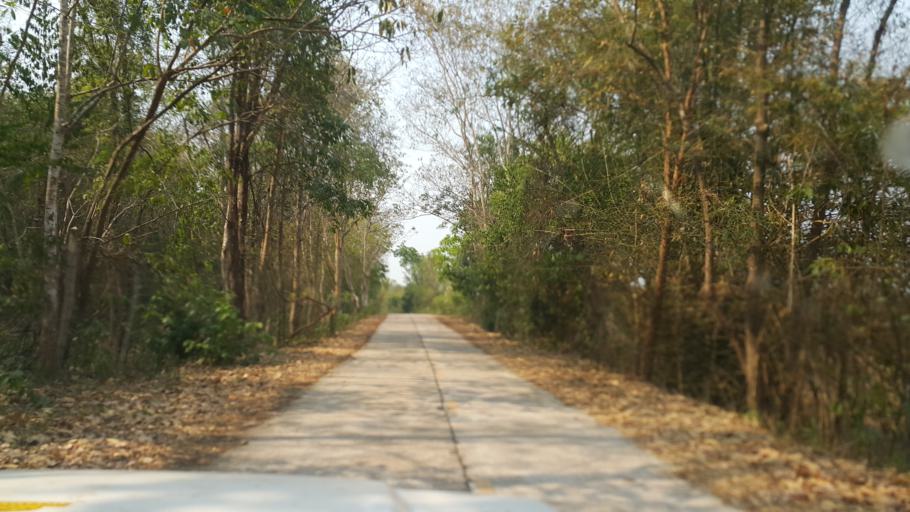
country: TH
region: Nakhon Phanom
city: Ban Phaeng
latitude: 17.9813
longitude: 104.1472
